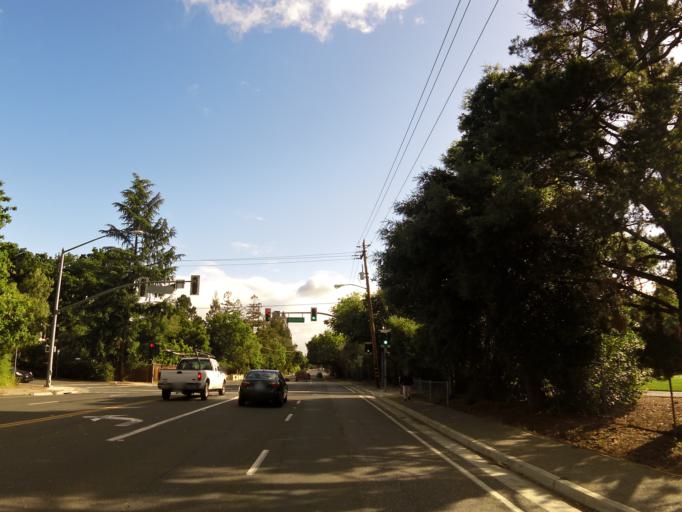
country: US
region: California
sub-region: Santa Clara County
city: Loyola
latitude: 37.3558
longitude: -122.1028
